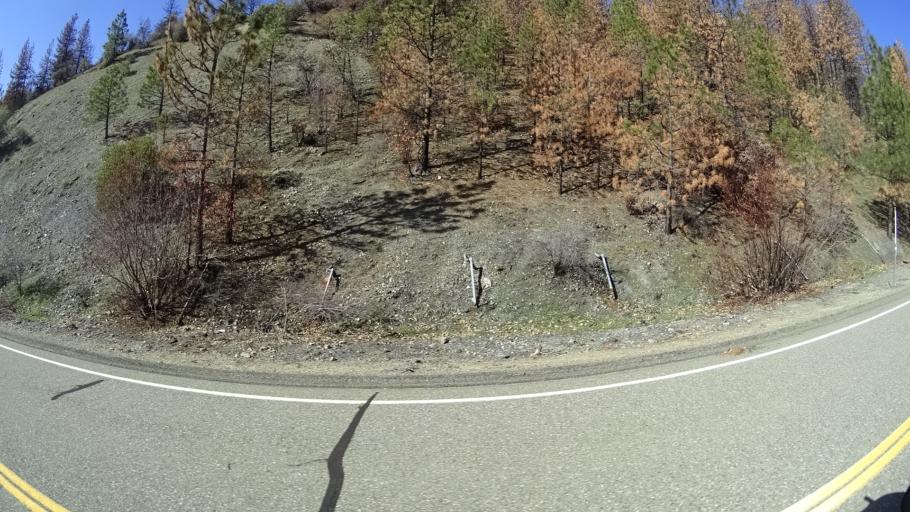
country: US
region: California
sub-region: Tehama County
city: Rancho Tehama Reserve
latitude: 39.6720
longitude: -122.6930
